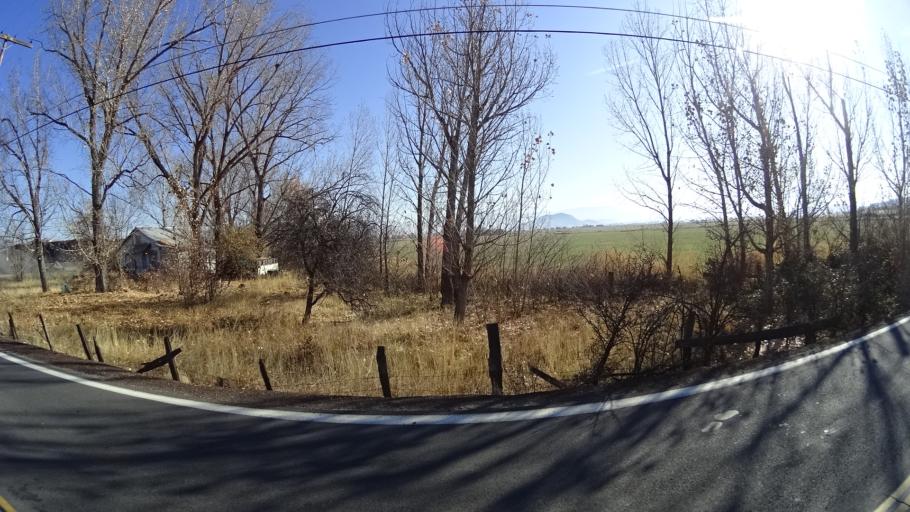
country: US
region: California
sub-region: Siskiyou County
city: Yreka
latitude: 41.7284
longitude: -122.5933
